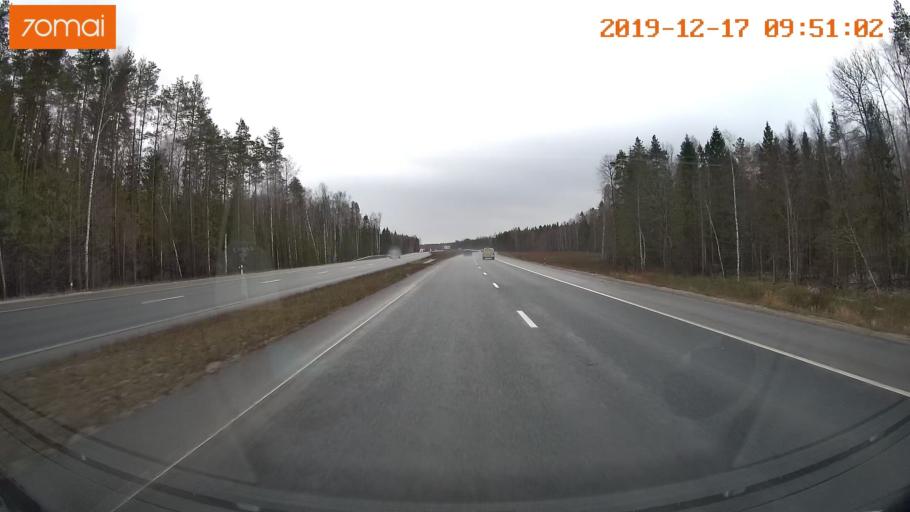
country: RU
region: Vladimir
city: Kommunar
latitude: 56.0497
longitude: 40.5164
